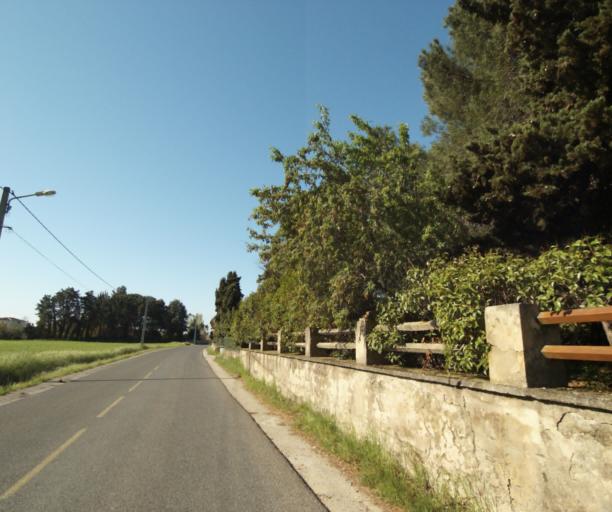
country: FR
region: Languedoc-Roussillon
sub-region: Departement de l'Herault
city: Castelnau-le-Lez
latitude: 43.6311
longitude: 3.9218
